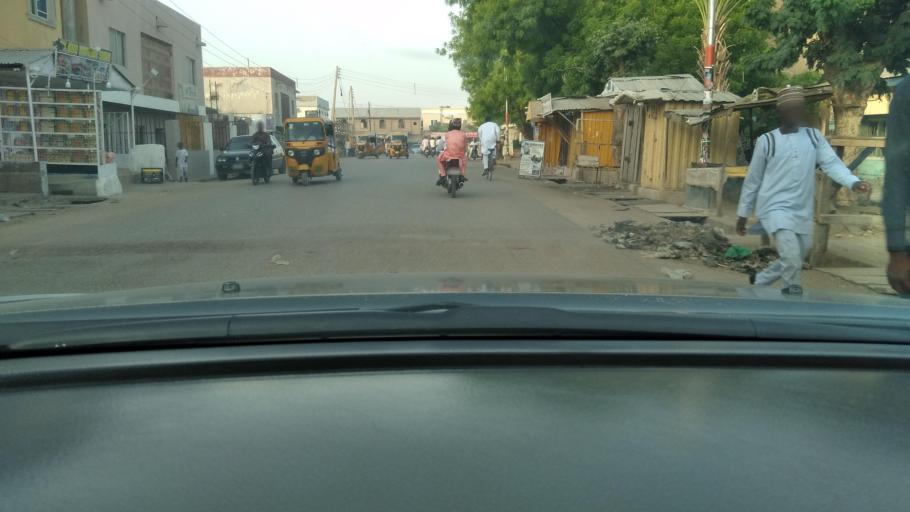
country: NG
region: Kano
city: Kano
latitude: 11.9617
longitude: 8.5258
